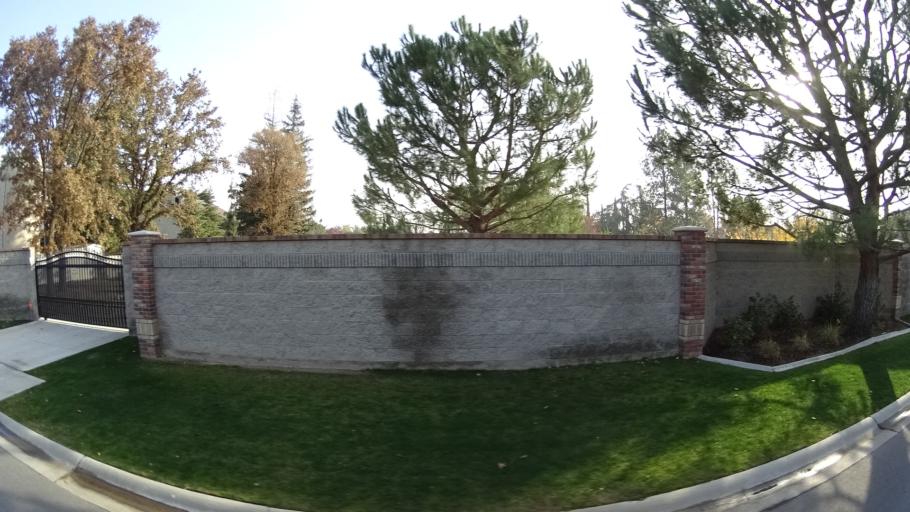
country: US
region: California
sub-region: Kern County
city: Greenacres
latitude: 35.4352
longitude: -119.1077
